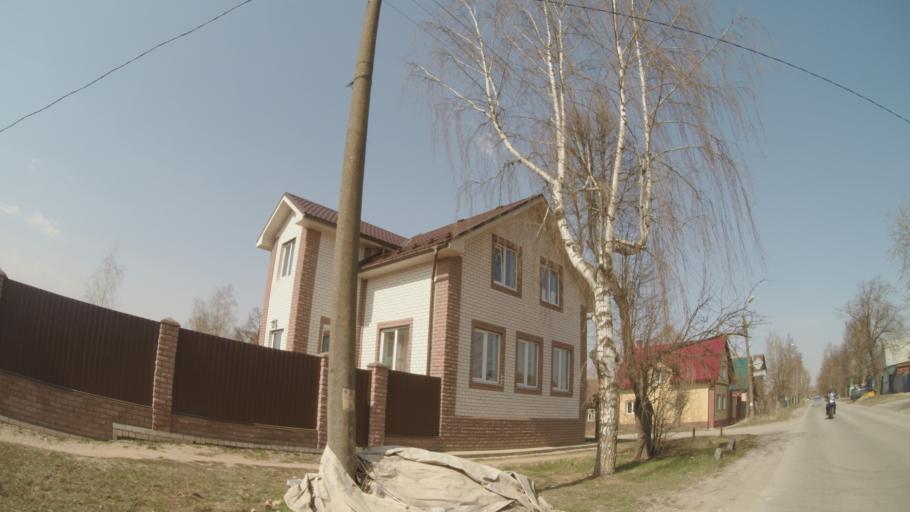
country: RU
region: Nizjnij Novgorod
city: Arzamas
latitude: 55.3903
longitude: 43.8254
